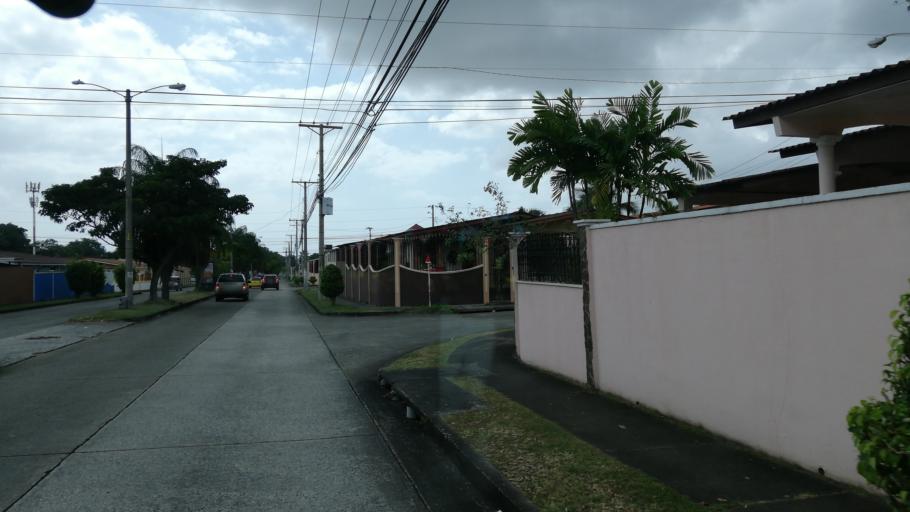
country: PA
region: Panama
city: San Miguelito
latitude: 9.0605
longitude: -79.4600
